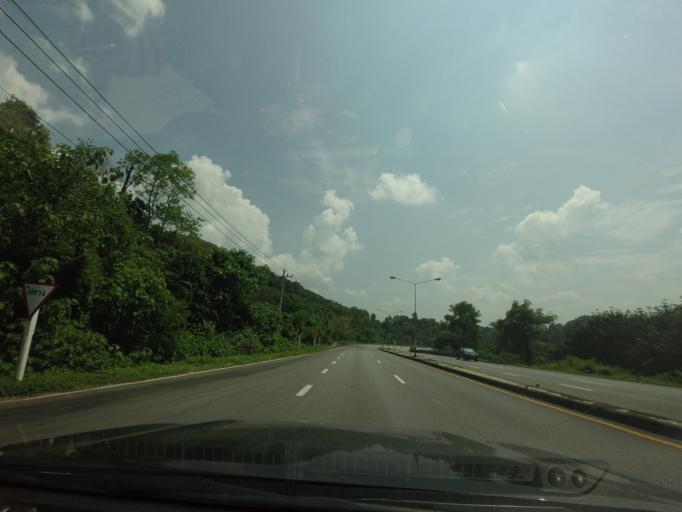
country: TH
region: Uttaradit
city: Lap Lae
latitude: 17.7765
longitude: 100.1284
